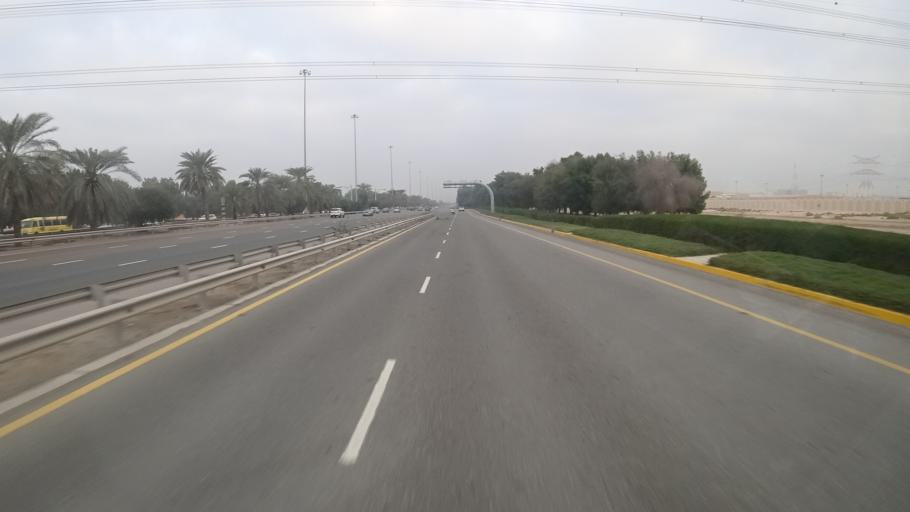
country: AE
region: Abu Dhabi
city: Abu Dhabi
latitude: 24.3316
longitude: 54.5834
